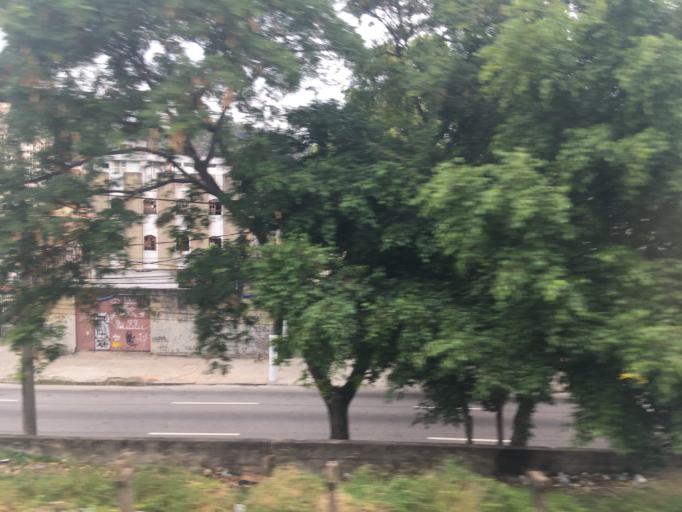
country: BR
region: Rio de Janeiro
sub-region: Rio De Janeiro
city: Rio de Janeiro
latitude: -22.9026
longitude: -43.2679
